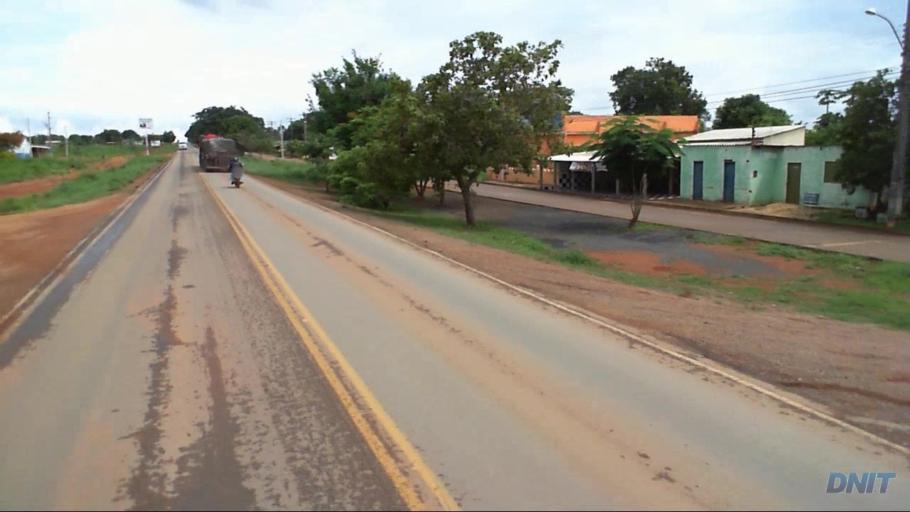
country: BR
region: Goias
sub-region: Padre Bernardo
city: Padre Bernardo
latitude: -15.2619
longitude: -48.2652
